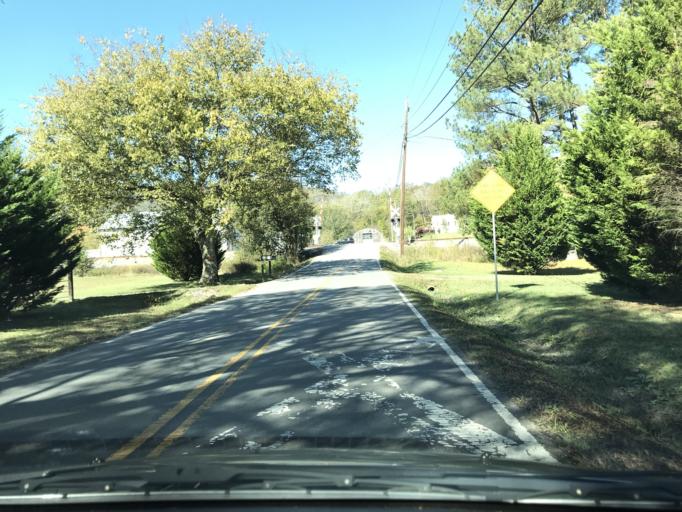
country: US
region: Georgia
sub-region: Dade County
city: Trenton
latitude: 34.9098
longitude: -85.4798
